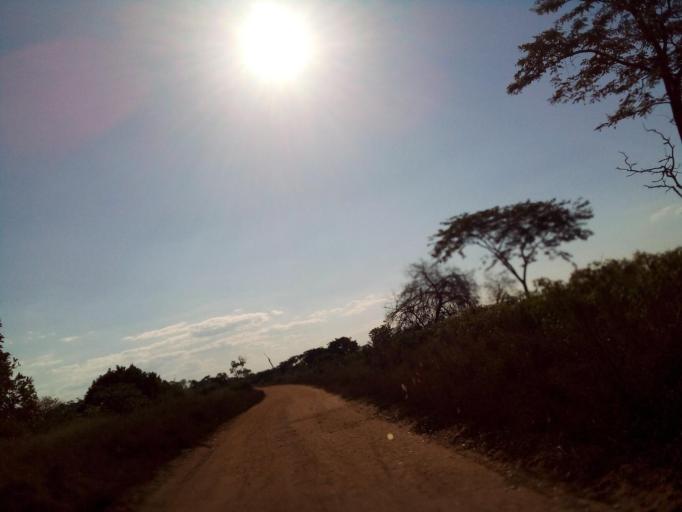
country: MZ
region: Zambezia
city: Quelimane
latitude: -17.4993
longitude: 36.5779
